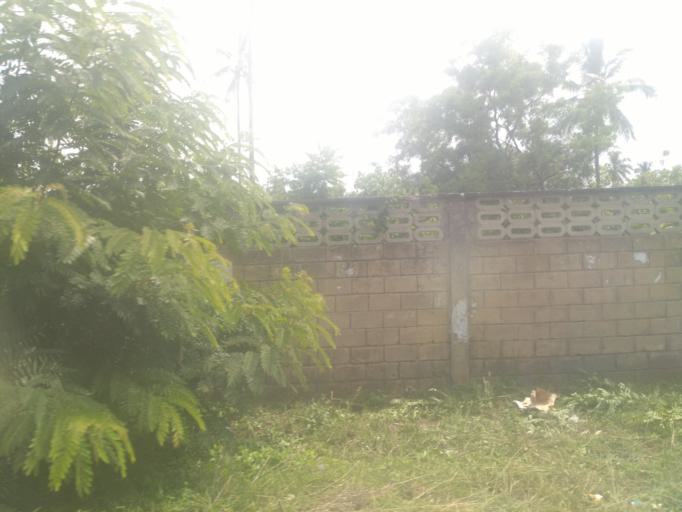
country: TZ
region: Zanzibar Urban/West
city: Zanzibar
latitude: -6.2307
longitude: 39.2118
